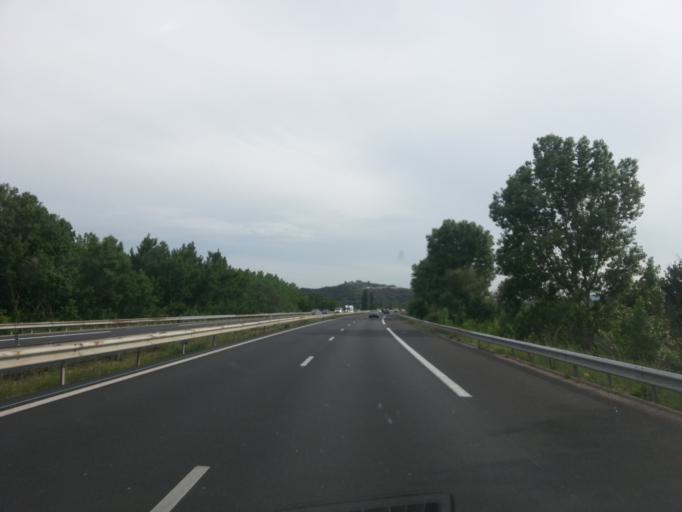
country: FR
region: Provence-Alpes-Cote d'Azur
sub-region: Departement du Vaucluse
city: Caderousse
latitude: 44.0962
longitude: 4.7876
